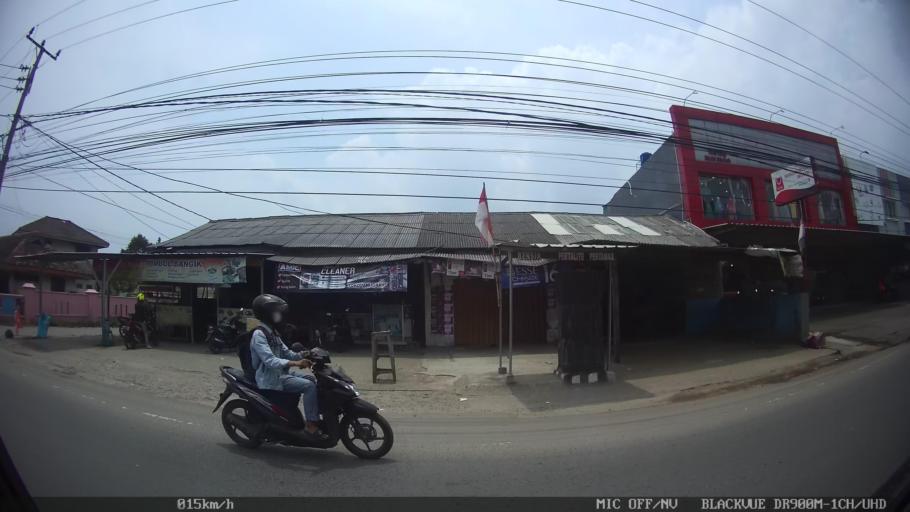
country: ID
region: Lampung
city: Kedaton
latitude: -5.3926
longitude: 105.2957
